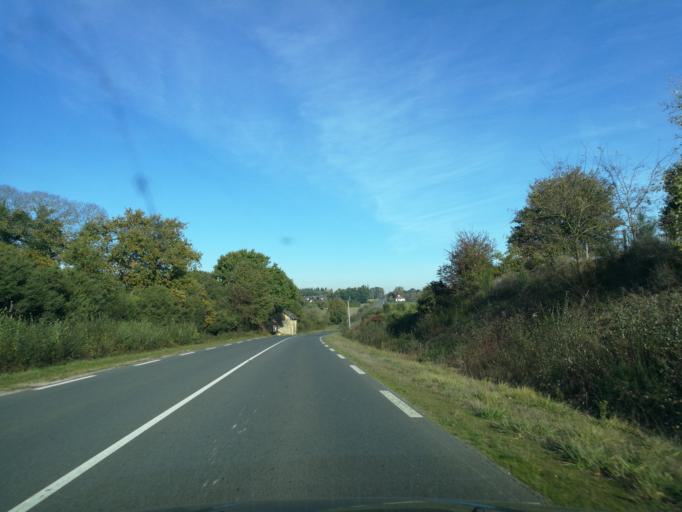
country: FR
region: Brittany
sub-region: Departement d'Ille-et-Vilaine
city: Bedee
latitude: 48.1623
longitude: -1.9455
